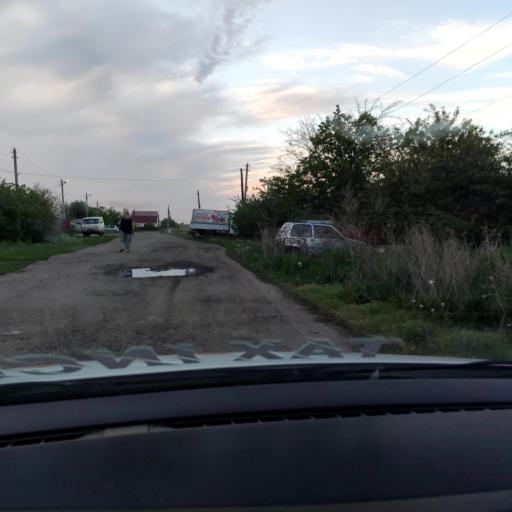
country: RU
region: Voronezj
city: Maslovka
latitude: 51.4550
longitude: 39.2379
